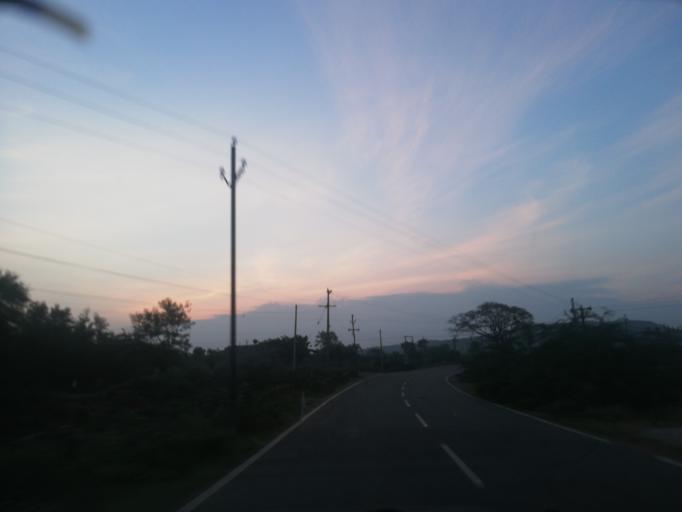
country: IN
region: Andhra Pradesh
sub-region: Guntur
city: Macherla
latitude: 16.6723
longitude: 79.2774
